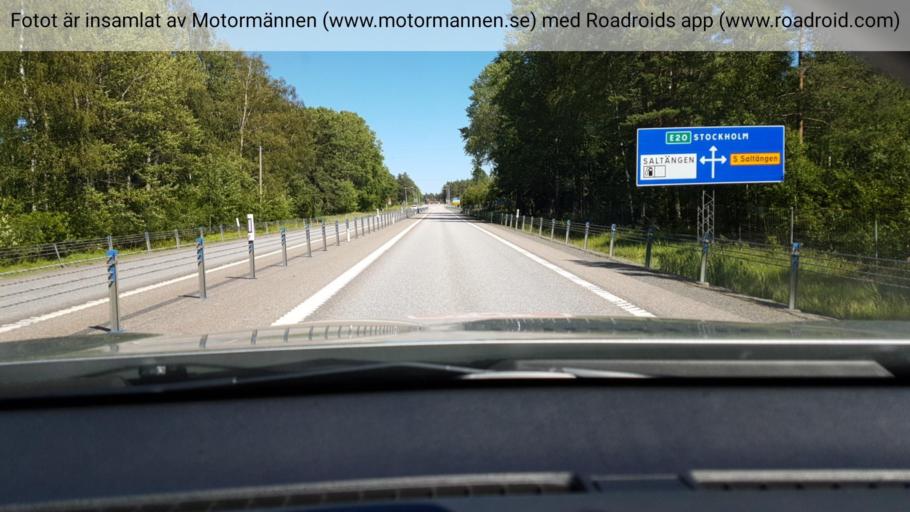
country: SE
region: OErebro
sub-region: Laxa Kommun
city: Laxa
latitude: 58.9790
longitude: 14.5999
